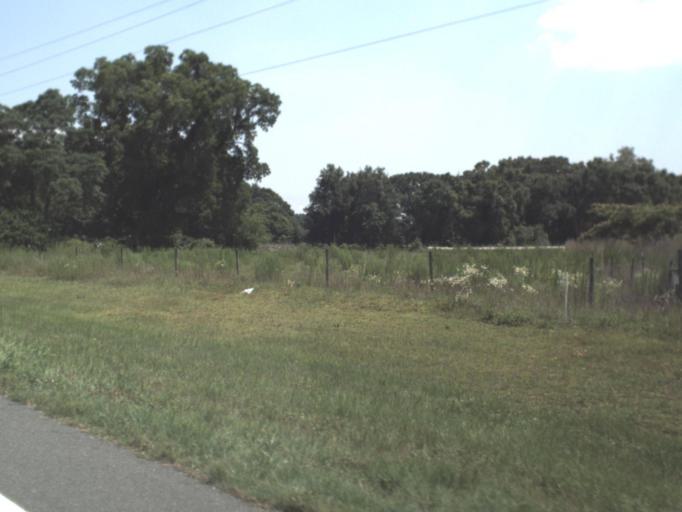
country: US
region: Florida
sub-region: Lafayette County
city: Mayo
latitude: 30.0875
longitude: -83.2252
